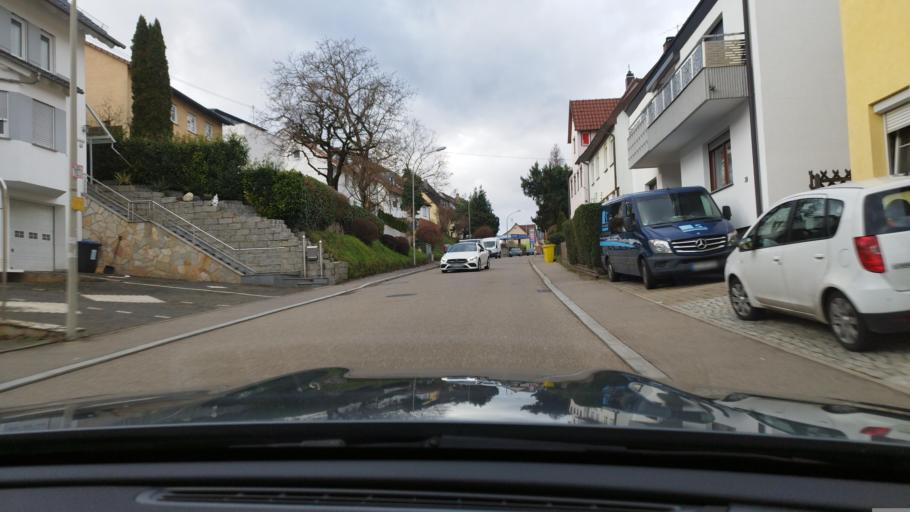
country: DE
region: Baden-Wuerttemberg
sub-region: Regierungsbezirk Stuttgart
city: Korb
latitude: 48.8408
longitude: 9.3580
